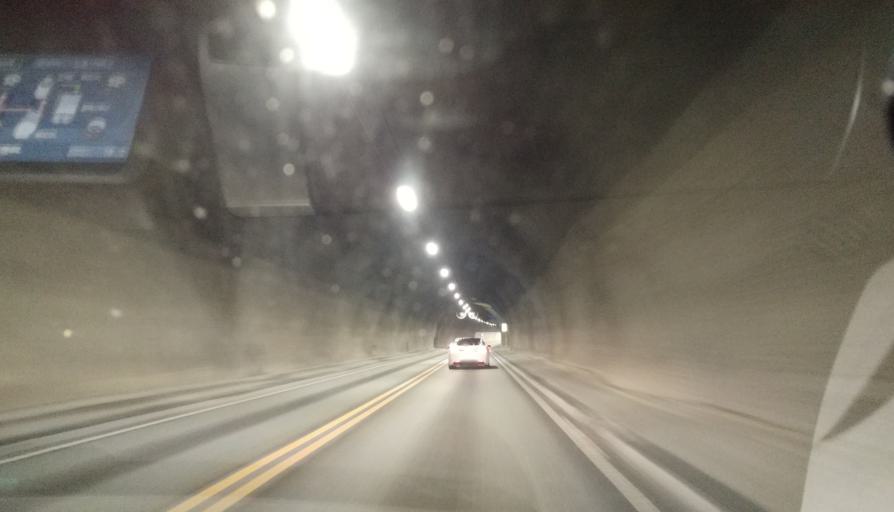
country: NO
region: Sor-Trondelag
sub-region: Malvik
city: Hommelvik
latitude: 63.4087
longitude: 10.7794
